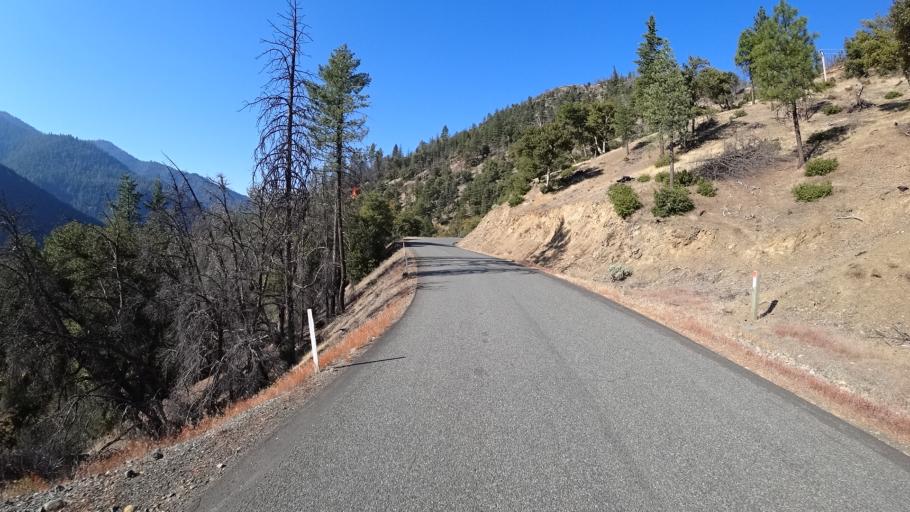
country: US
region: California
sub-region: Siskiyou County
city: Happy Camp
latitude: 41.7098
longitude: -123.0289
